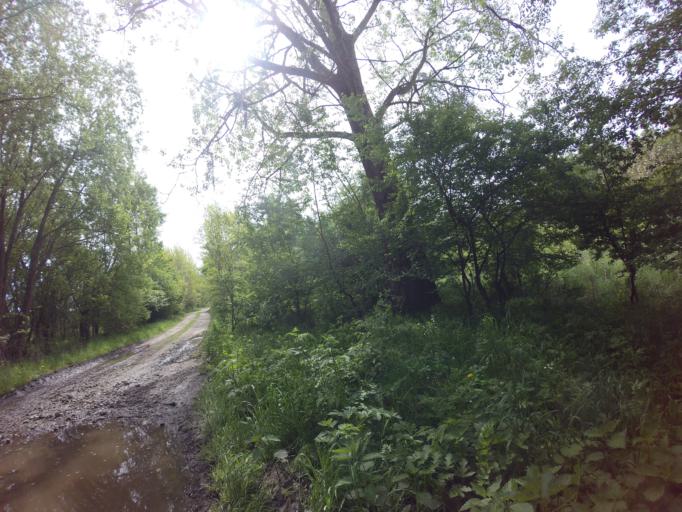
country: PL
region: West Pomeranian Voivodeship
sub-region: Powiat choszczenski
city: Recz
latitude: 53.1610
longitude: 15.5693
